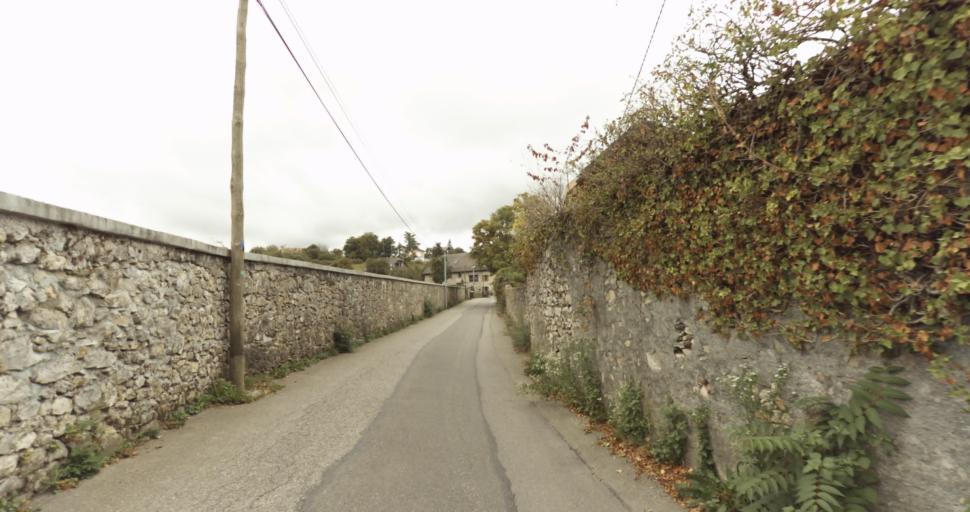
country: FR
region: Rhone-Alpes
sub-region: Departement de la Savoie
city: La Ravoire
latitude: 45.5640
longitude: 5.9610
